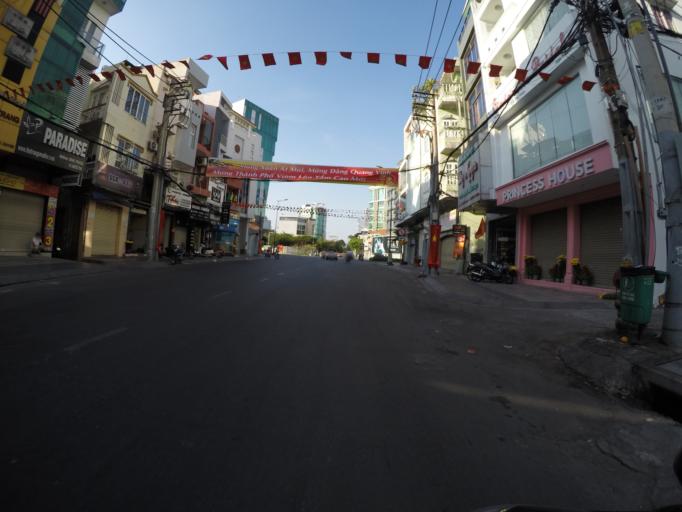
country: VN
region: Ho Chi Minh City
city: Quan Phu Nhuan
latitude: 10.7934
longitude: 106.6779
